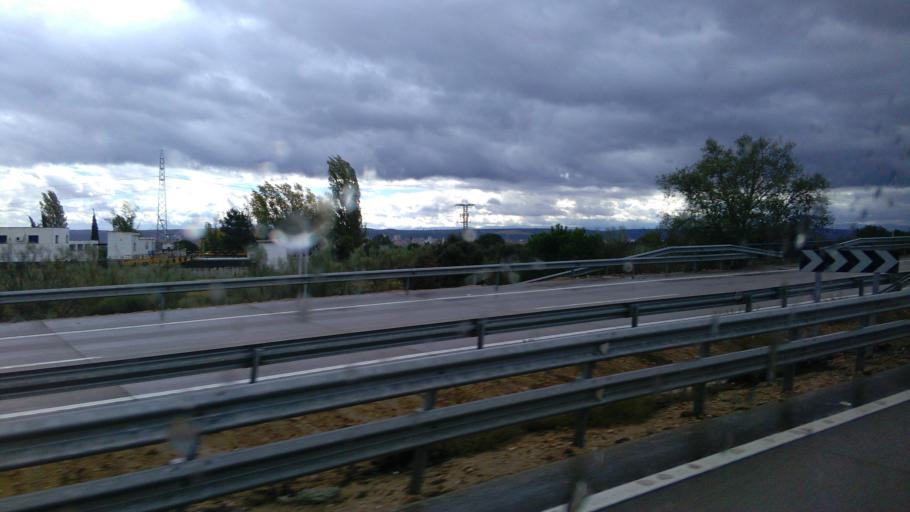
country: ES
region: Castille-La Mancha
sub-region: Province of Toledo
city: Talavera de la Reina
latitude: 39.9905
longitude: -4.8391
